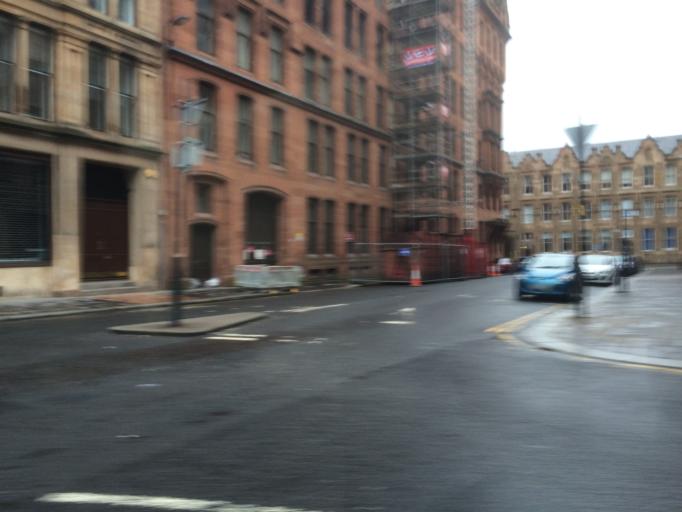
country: GB
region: Scotland
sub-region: Glasgow City
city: Glasgow
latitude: 55.8602
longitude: -4.2460
